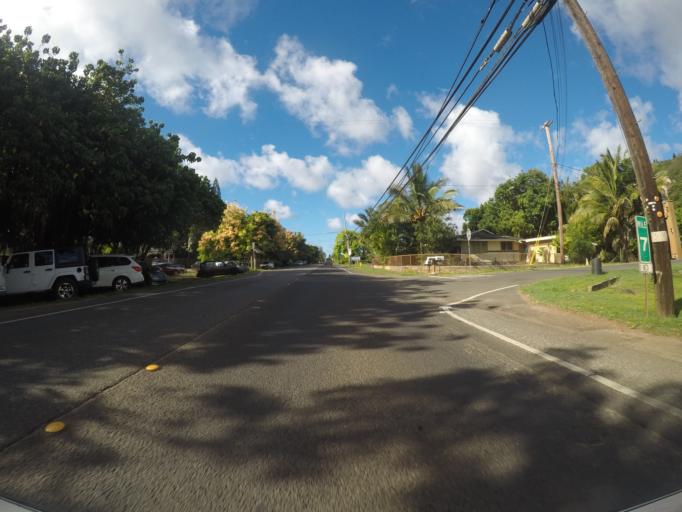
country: US
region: Hawaii
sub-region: Honolulu County
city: Pupukea
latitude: 21.6549
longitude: -158.0594
